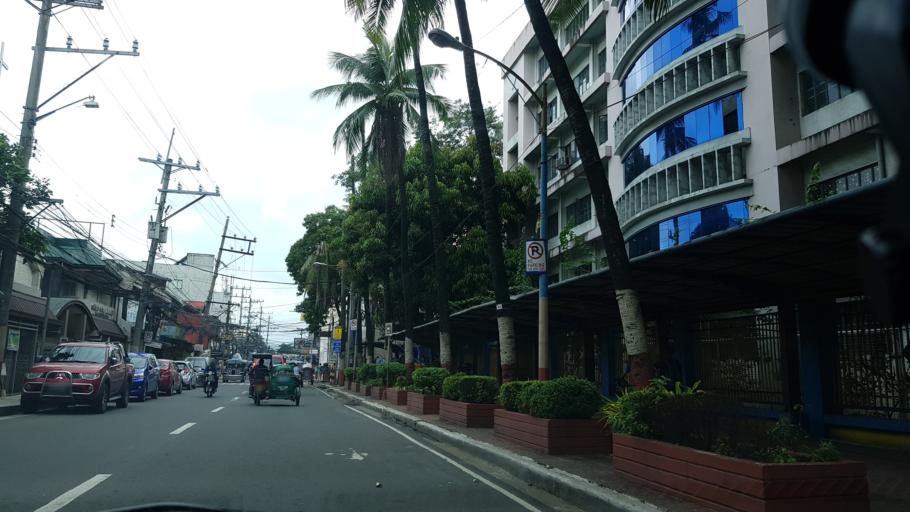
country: PH
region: Metro Manila
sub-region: Pasig
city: Pasig City
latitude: 14.5674
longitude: 121.0763
